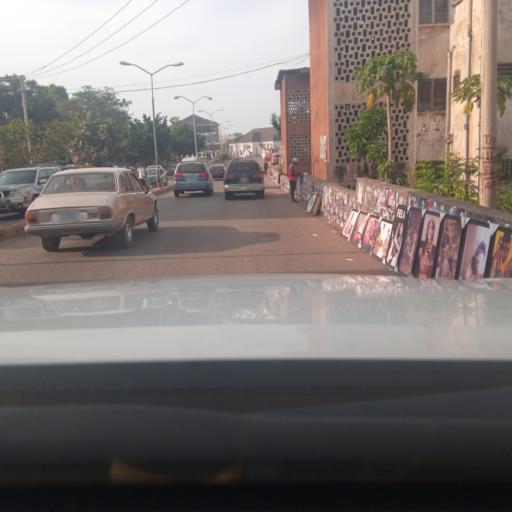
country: NG
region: Enugu
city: Enugu
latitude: 6.4534
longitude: 7.5043
